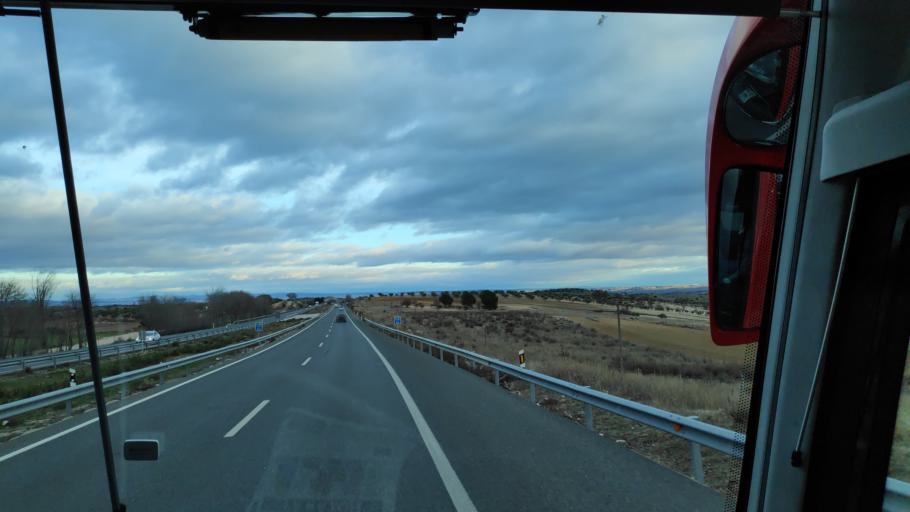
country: ES
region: Madrid
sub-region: Provincia de Madrid
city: Villarejo de Salvanes
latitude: 40.1523
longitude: -3.2463
